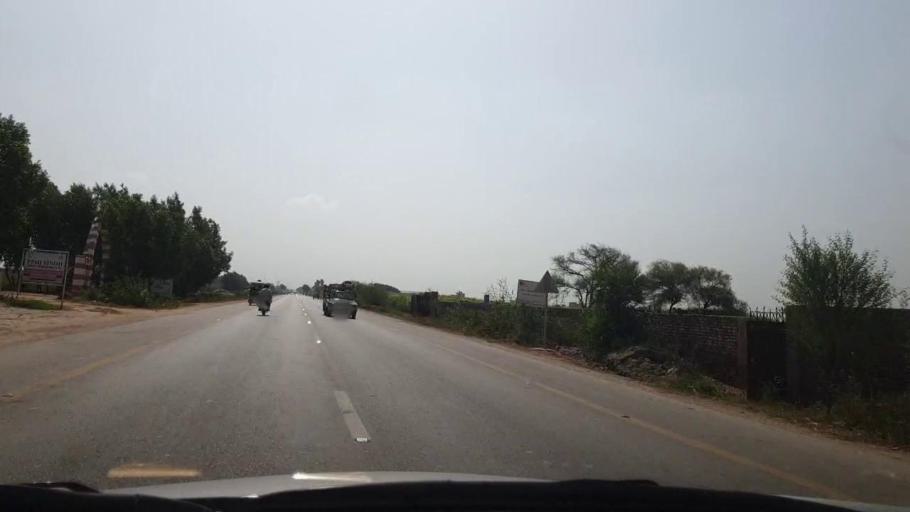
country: PK
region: Sindh
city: Matli
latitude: 25.0643
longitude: 68.6314
